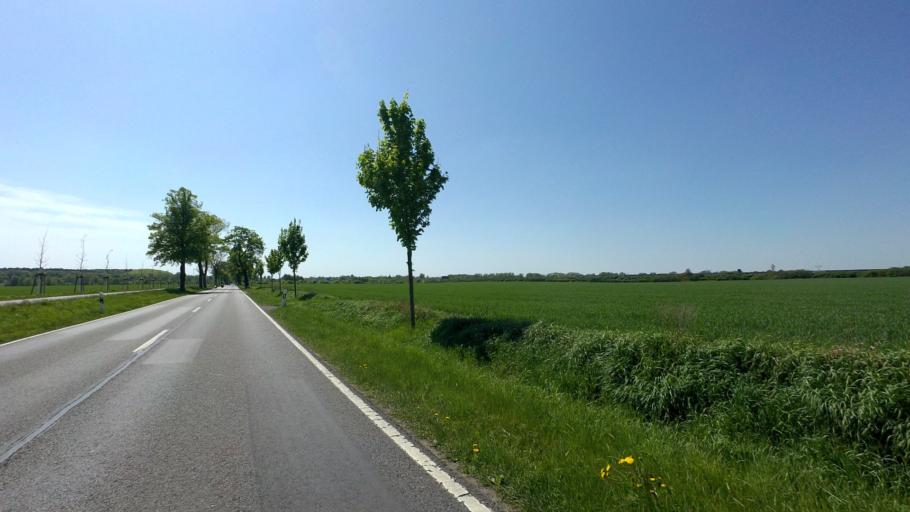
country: DE
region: Brandenburg
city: Schulzendorf
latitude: 52.3567
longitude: 13.5574
